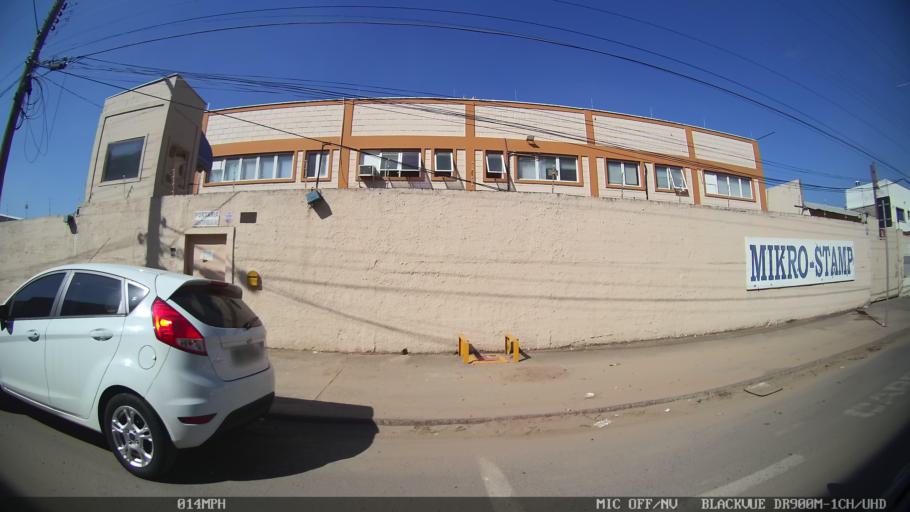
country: BR
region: Sao Paulo
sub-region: Campinas
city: Campinas
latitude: -22.9431
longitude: -47.0871
